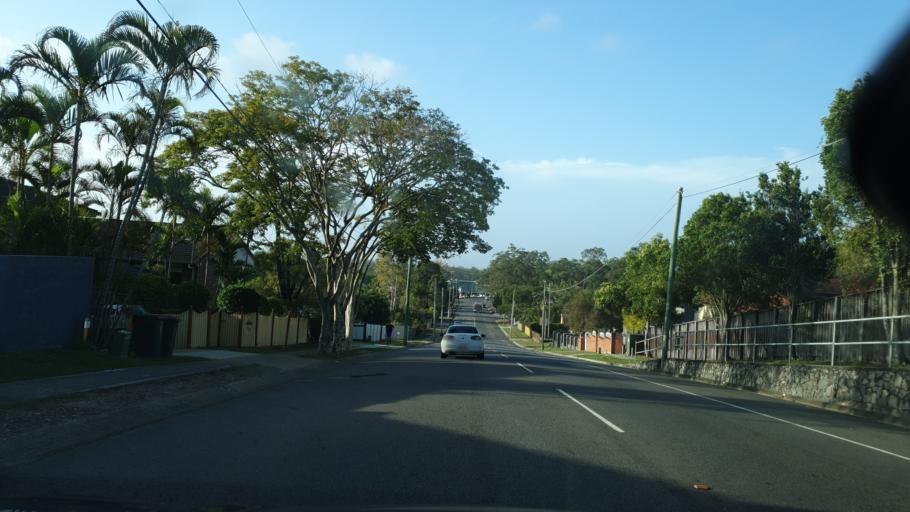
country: AU
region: Queensland
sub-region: Brisbane
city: Belmont
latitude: -27.4882
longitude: 153.1272
